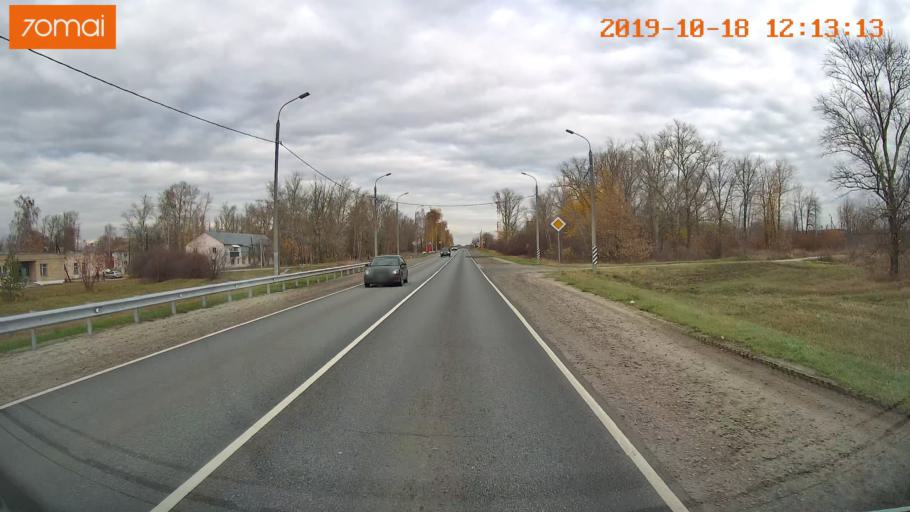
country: RU
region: Rjazan
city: Zakharovo
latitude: 54.4194
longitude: 39.3679
